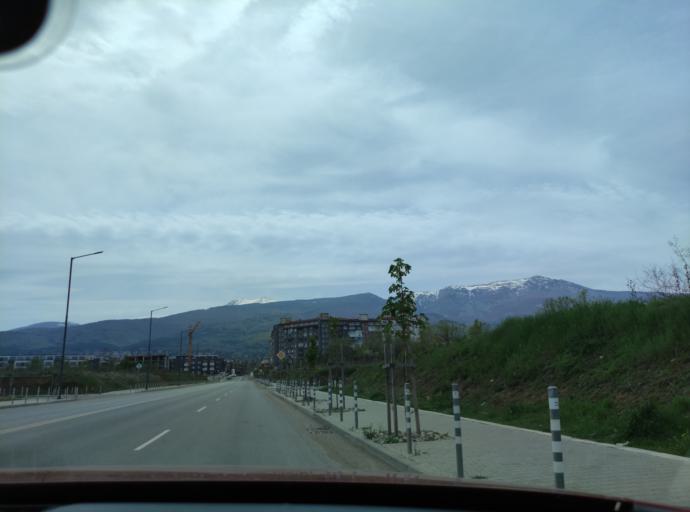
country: BG
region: Sofia-Capital
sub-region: Stolichna Obshtina
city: Sofia
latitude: 42.6398
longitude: 23.3432
